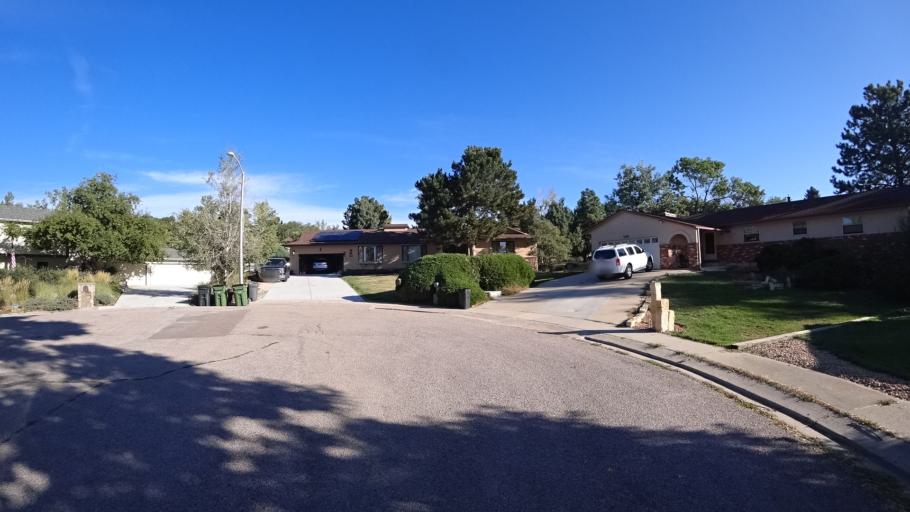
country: US
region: Colorado
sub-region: El Paso County
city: Cimarron Hills
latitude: 38.9109
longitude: -104.7571
